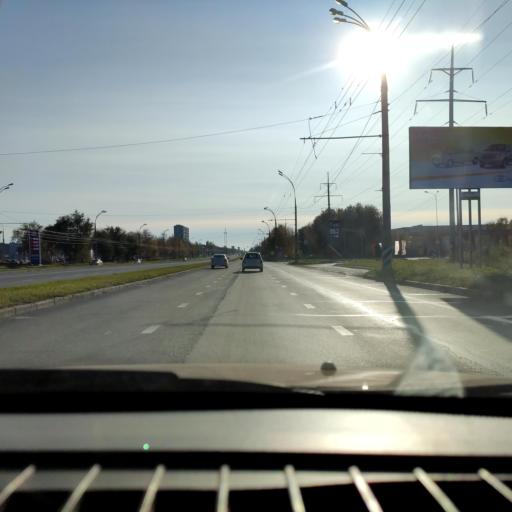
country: RU
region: Samara
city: Tol'yatti
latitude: 53.5465
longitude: 49.2652
